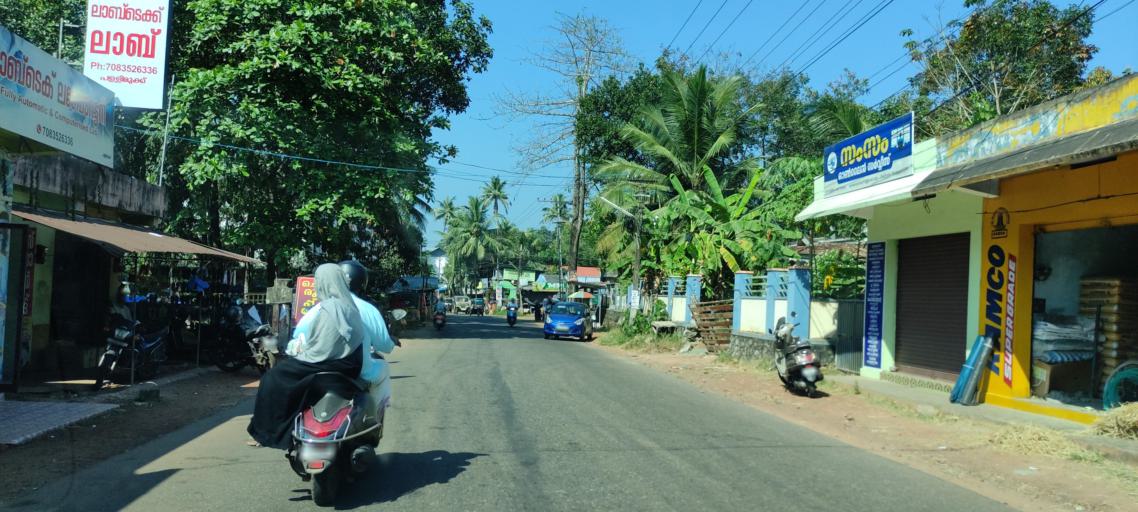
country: IN
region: Kerala
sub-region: Kollam
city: Panmana
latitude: 9.0421
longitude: 76.5881
